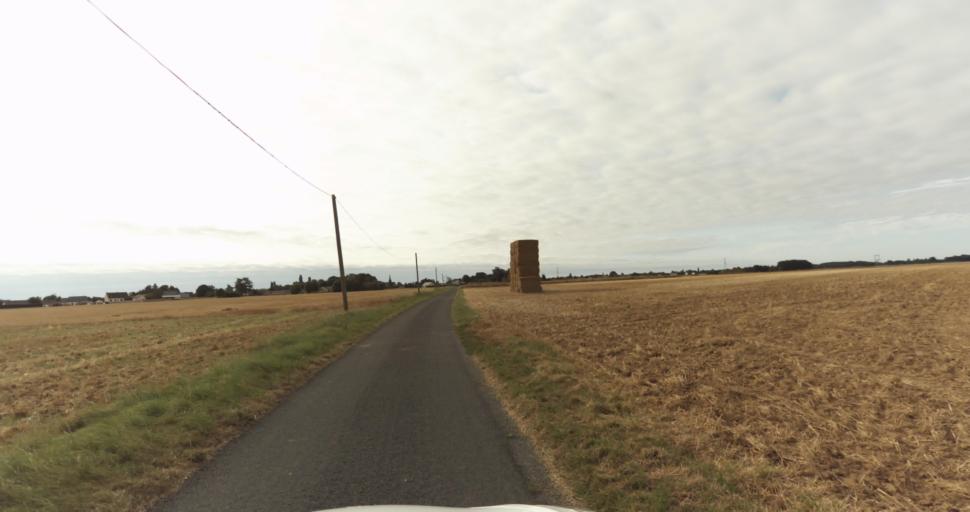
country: FR
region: Haute-Normandie
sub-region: Departement de l'Eure
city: La Madeleine-de-Nonancourt
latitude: 48.8713
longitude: 1.2407
